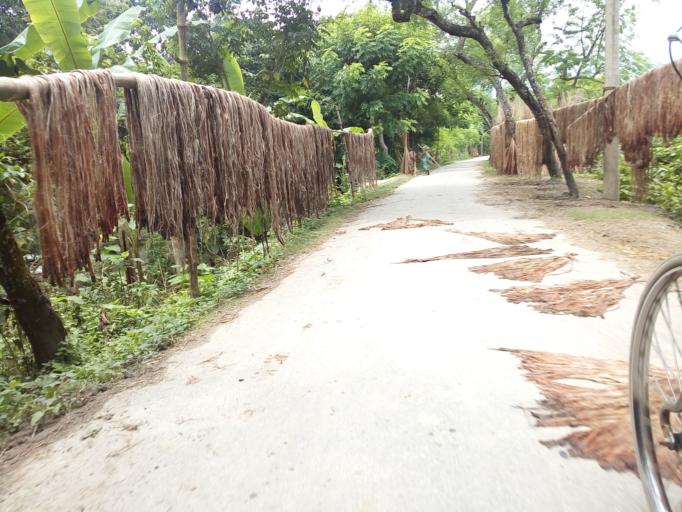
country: BD
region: Khulna
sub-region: Magura
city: Magura
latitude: 23.5262
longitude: 89.5533
